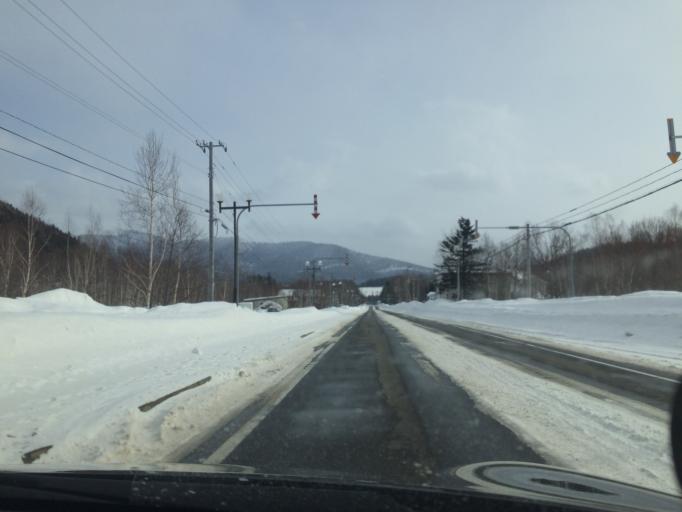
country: JP
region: Hokkaido
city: Shimo-furano
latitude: 43.0489
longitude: 142.6481
